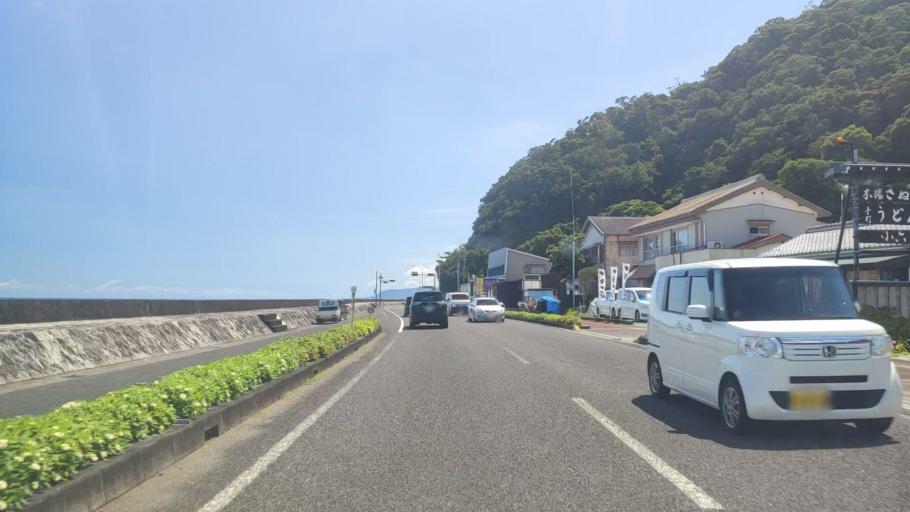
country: JP
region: Wakayama
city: Shingu
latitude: 33.8809
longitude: 136.0948
